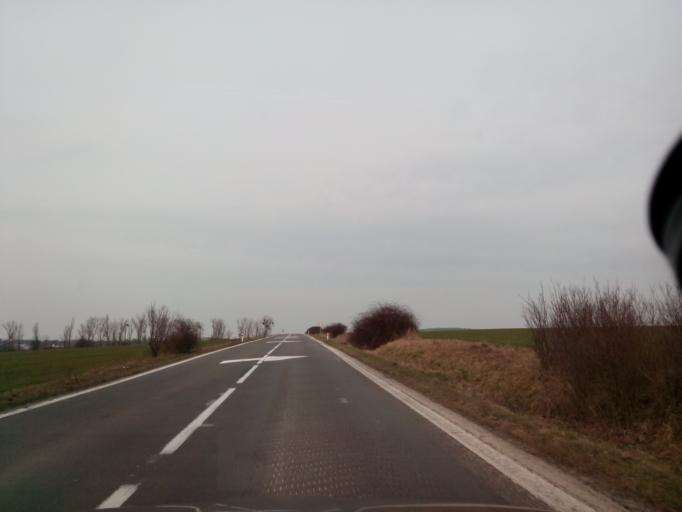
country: HU
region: Borsod-Abauj-Zemplen
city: Satoraljaujhely
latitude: 48.4751
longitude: 21.6418
